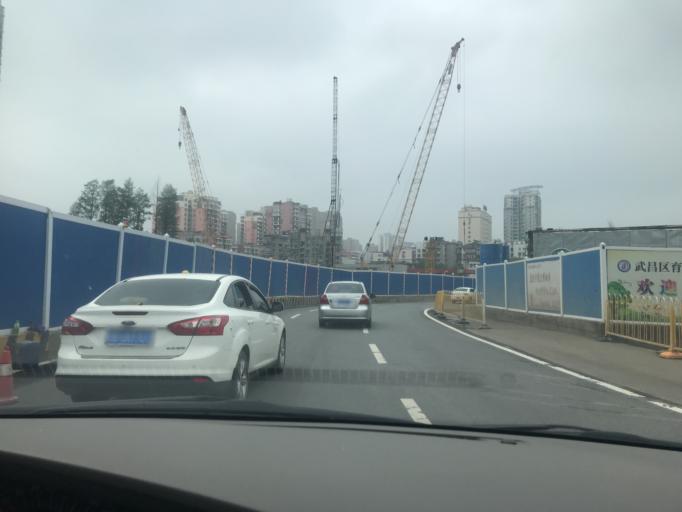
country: CN
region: Hubei
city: Jiang'an
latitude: 30.5927
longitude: 114.3273
